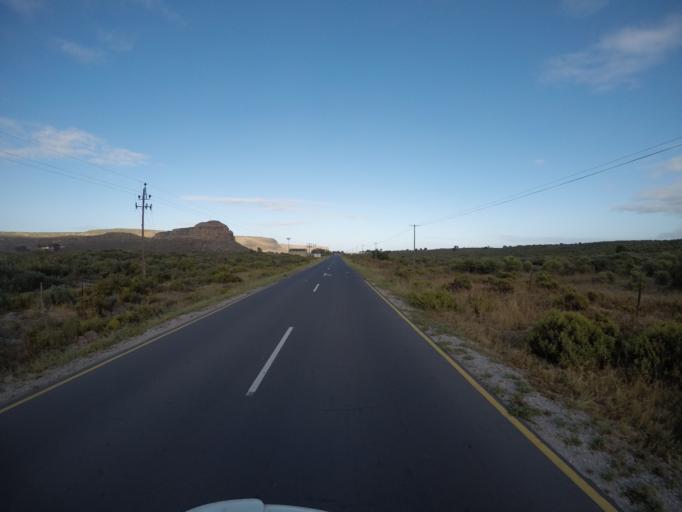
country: ZA
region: Western Cape
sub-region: West Coast District Municipality
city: Clanwilliam
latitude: -32.3127
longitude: 18.3651
